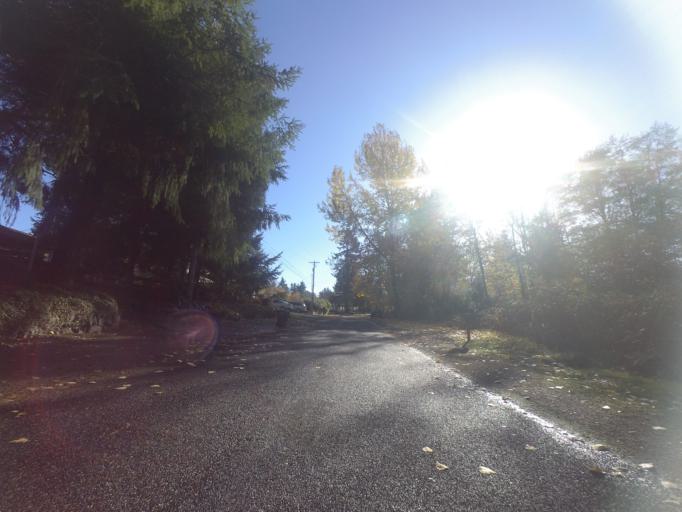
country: US
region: Washington
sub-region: Pierce County
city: University Place
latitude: 47.2330
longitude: -122.5565
